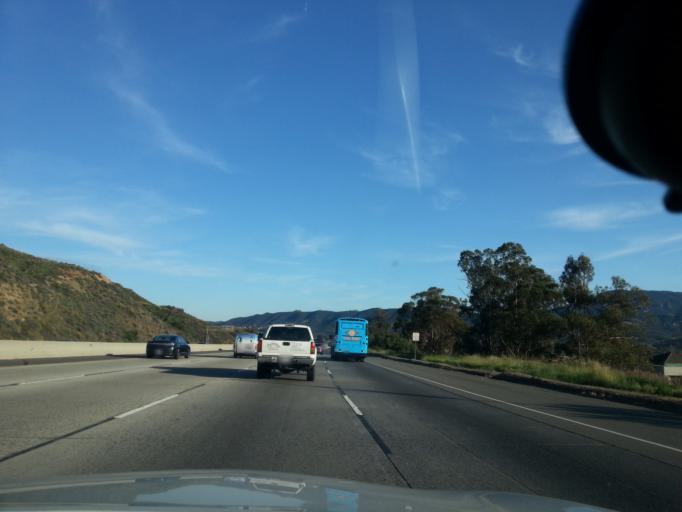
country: US
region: California
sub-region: Ventura County
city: Casa Conejo
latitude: 34.1974
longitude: -118.9531
